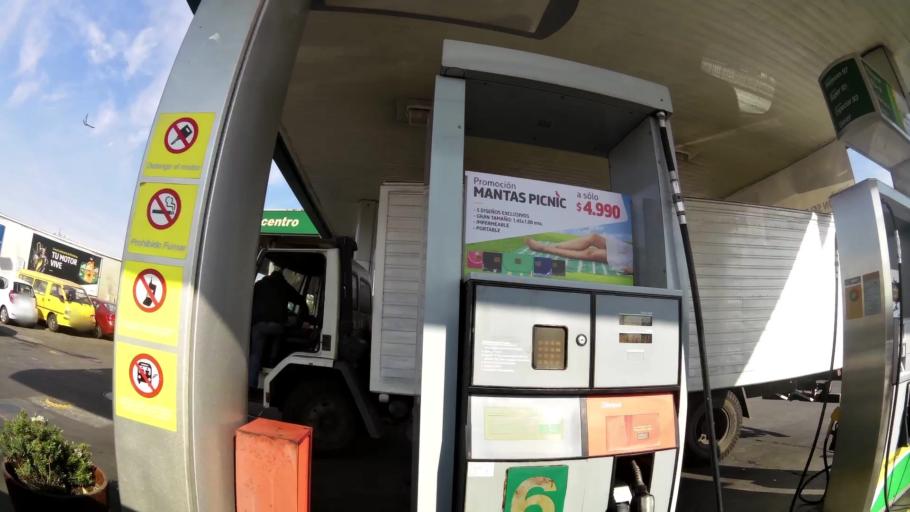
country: CL
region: Santiago Metropolitan
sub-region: Provincia de Santiago
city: Santiago
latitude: -33.5133
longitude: -70.6375
